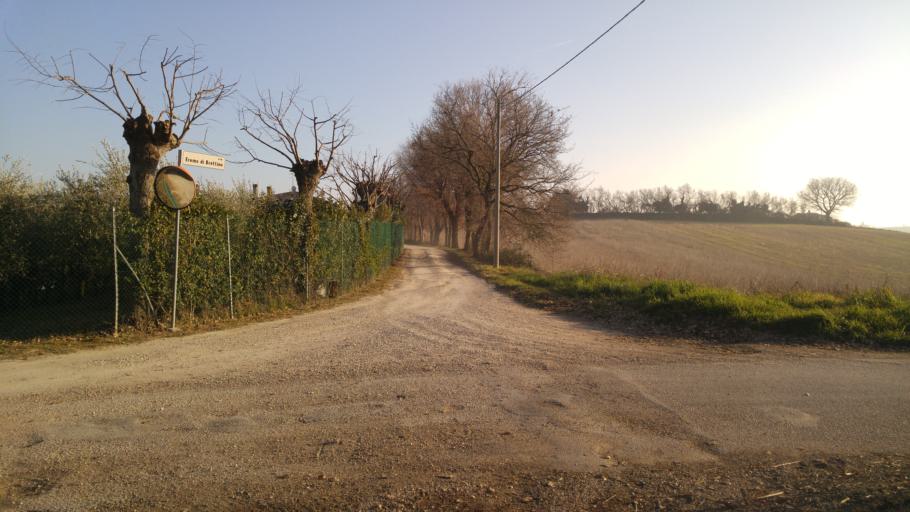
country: IT
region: The Marches
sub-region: Provincia di Pesaro e Urbino
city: Fenile
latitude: 43.8572
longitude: 12.9593
